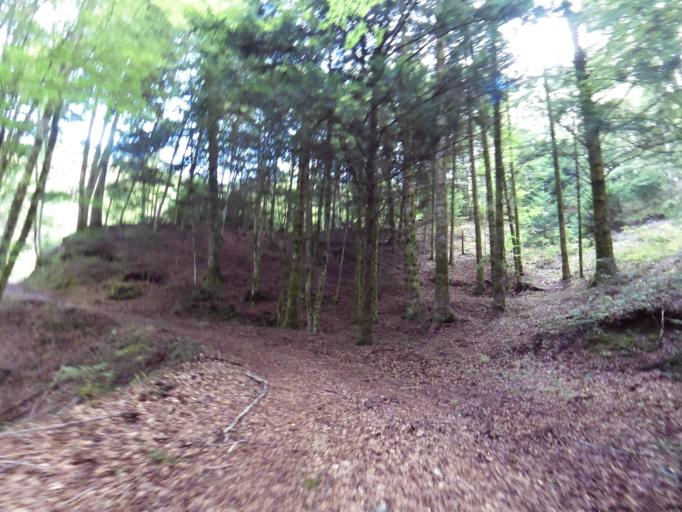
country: IT
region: Calabria
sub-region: Provincia di Vibo-Valentia
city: Mongiana
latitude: 38.5232
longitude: 16.3796
